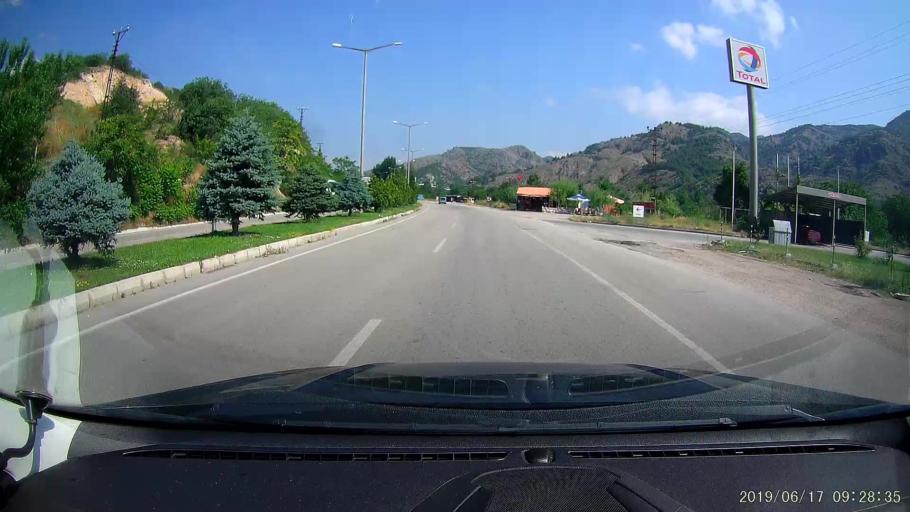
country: TR
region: Amasya
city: Amasya
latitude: 40.6900
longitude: 35.8218
